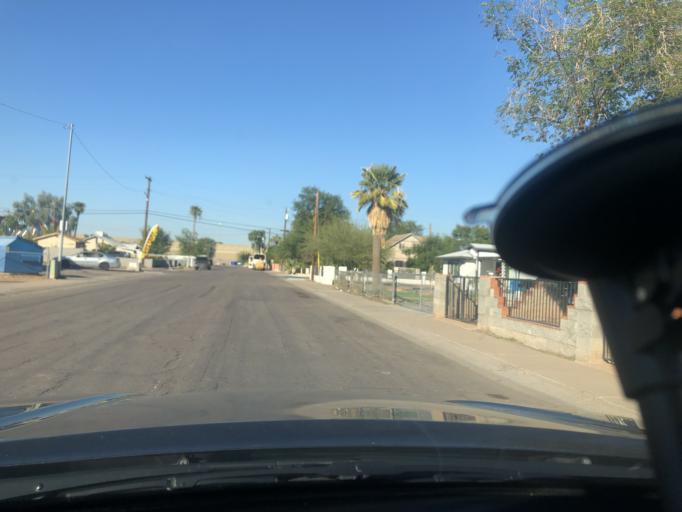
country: US
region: Arizona
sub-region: Maricopa County
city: Phoenix
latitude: 33.4599
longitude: -112.0259
